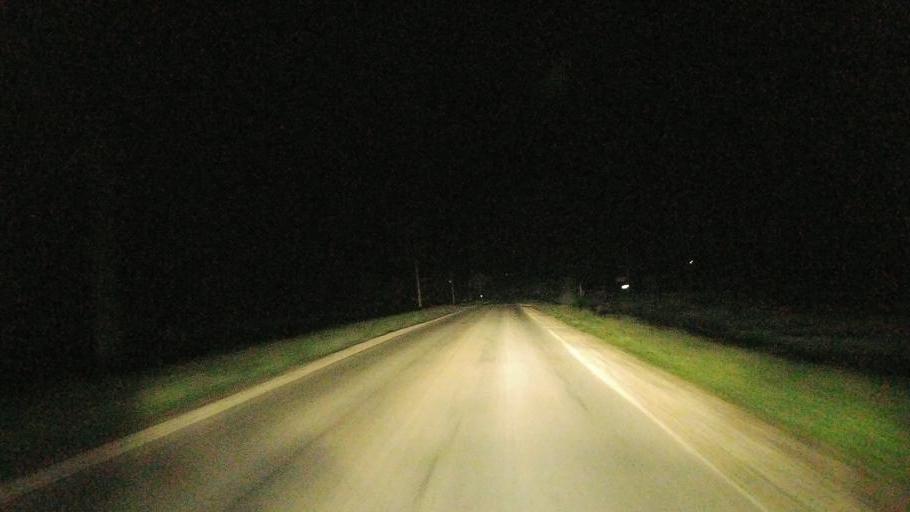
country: US
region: Iowa
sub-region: Decatur County
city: Lamoni
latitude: 40.6240
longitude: -94.0331
